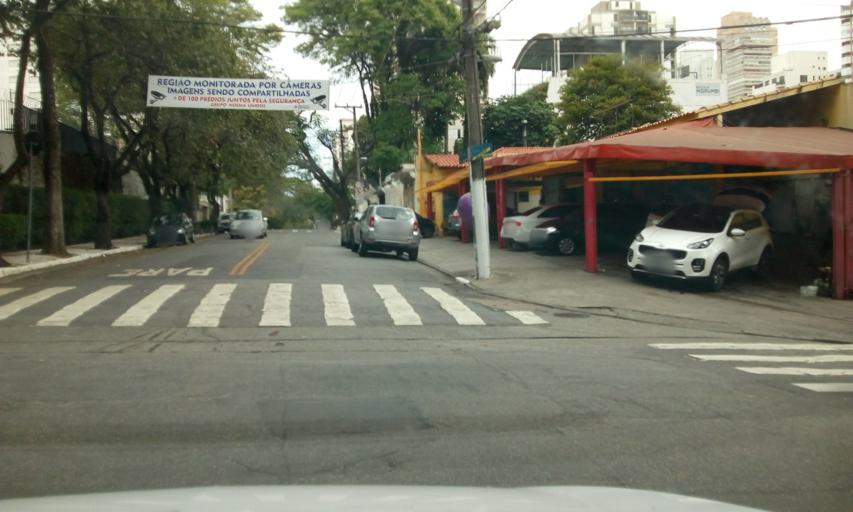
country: BR
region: Sao Paulo
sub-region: Sao Paulo
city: Sao Paulo
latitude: -23.6089
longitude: -46.6565
